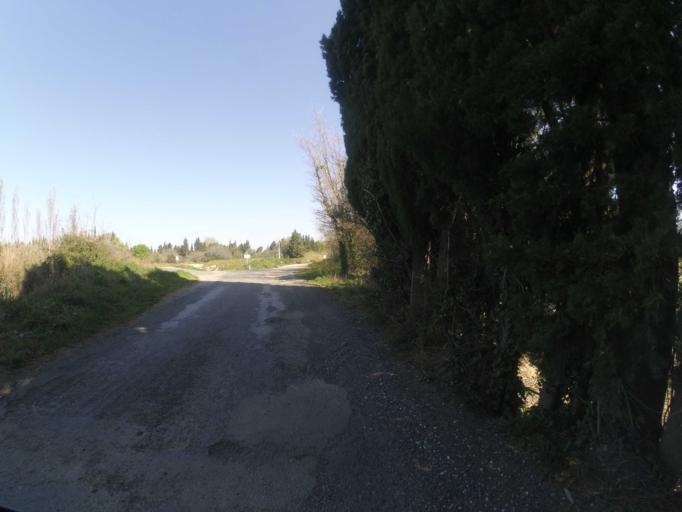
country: FR
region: Languedoc-Roussillon
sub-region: Departement des Pyrenees-Orientales
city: Pezilla-la-Riviere
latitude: 42.6670
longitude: 2.7600
